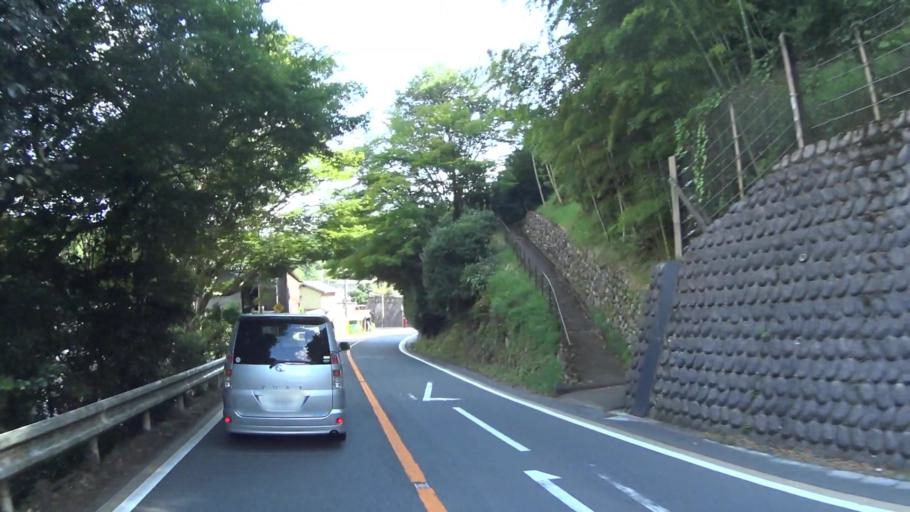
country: JP
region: Kyoto
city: Kyoto
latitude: 35.0469
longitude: 135.6812
